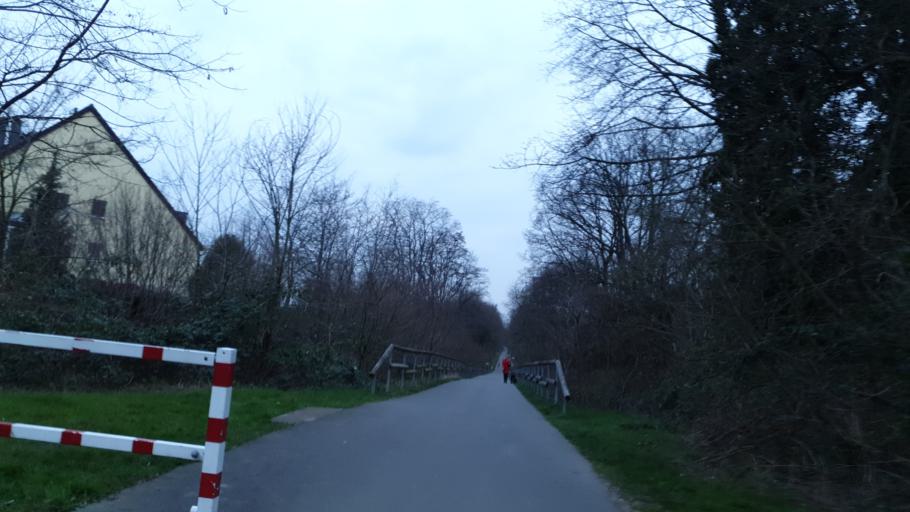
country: DE
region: North Rhine-Westphalia
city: Burscheid
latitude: 51.0839
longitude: 7.1038
